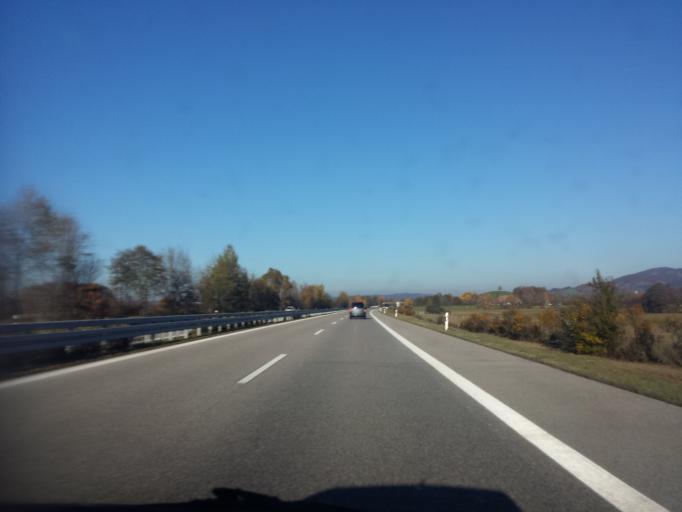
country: DE
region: Bavaria
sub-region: Upper Bavaria
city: Eschenlohe
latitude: 47.6149
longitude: 11.1854
